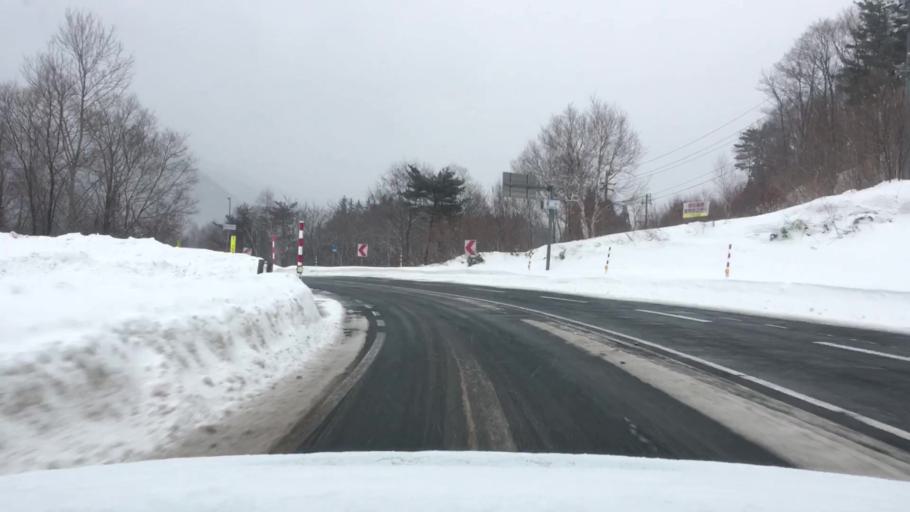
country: JP
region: Akita
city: Hanawa
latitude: 40.0307
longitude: 140.9867
